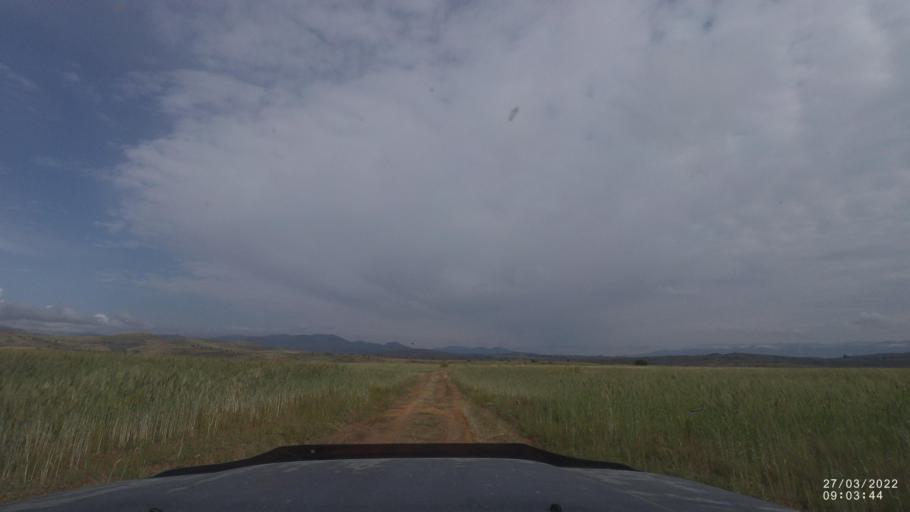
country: BO
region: Cochabamba
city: Cliza
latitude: -17.7360
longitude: -65.8621
